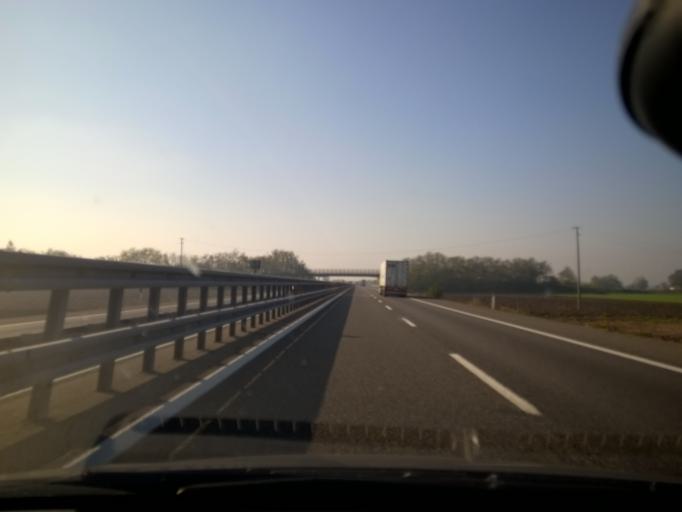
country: IT
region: Lombardy
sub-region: Provincia di Pavia
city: Broni
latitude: 45.0743
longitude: 9.2532
